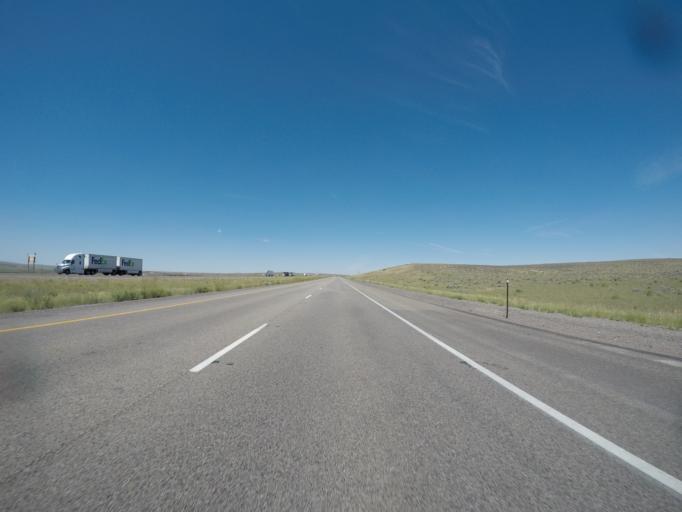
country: US
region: Wyoming
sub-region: Carbon County
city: Saratoga
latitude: 41.7430
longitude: -106.7806
